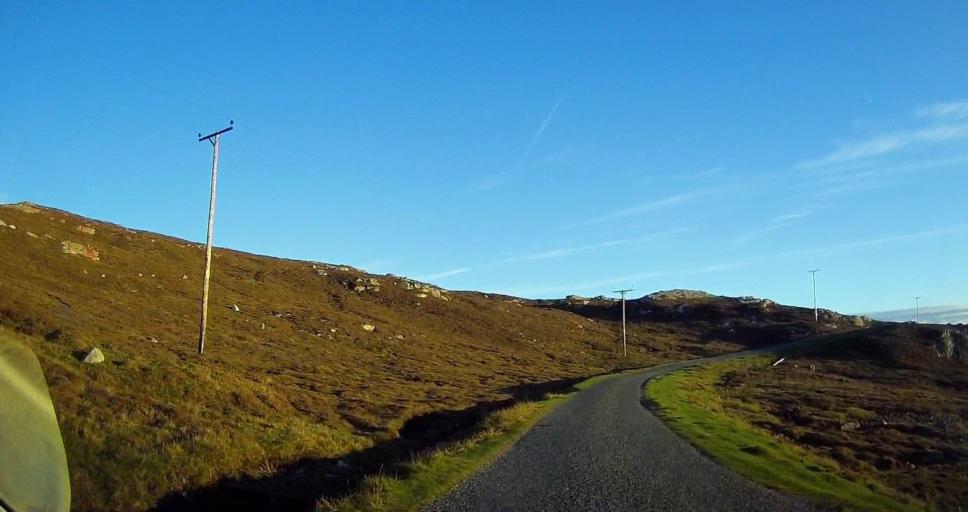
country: GB
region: Scotland
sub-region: Shetland Islands
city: Lerwick
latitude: 60.4459
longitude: -1.4336
